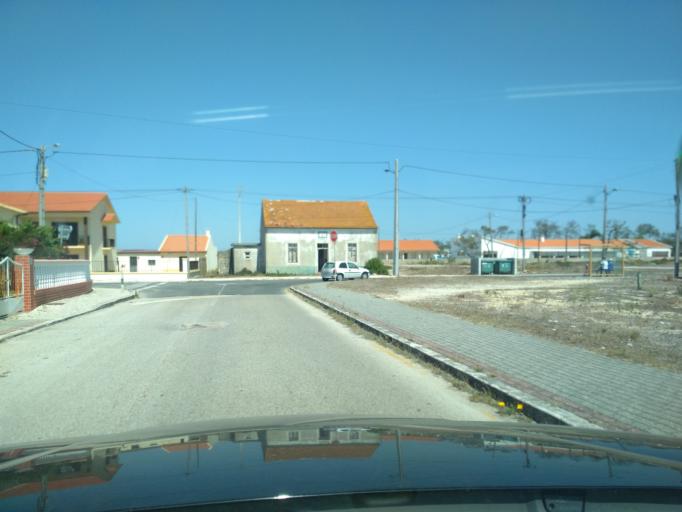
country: PT
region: Coimbra
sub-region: Figueira da Foz
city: Lavos
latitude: 40.0561
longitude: -8.8848
